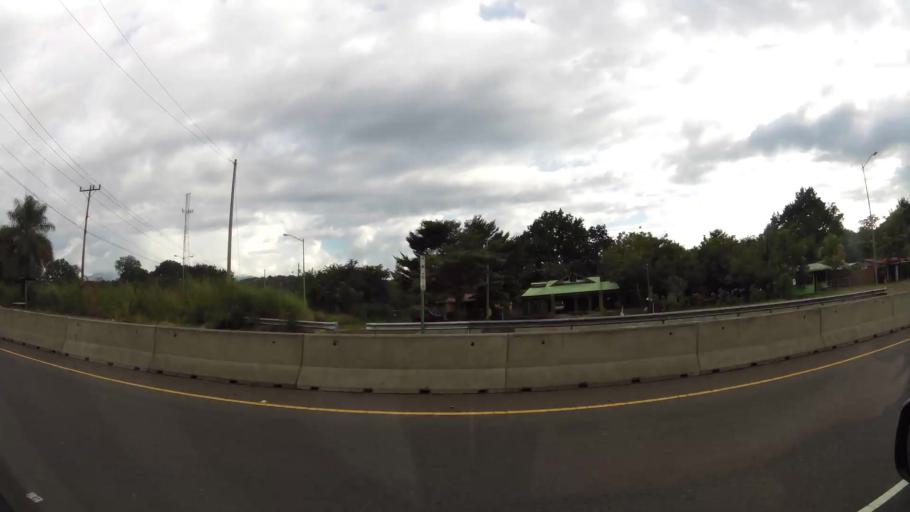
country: CR
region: Alajuela
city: Orotina
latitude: 9.8869
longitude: -84.5770
